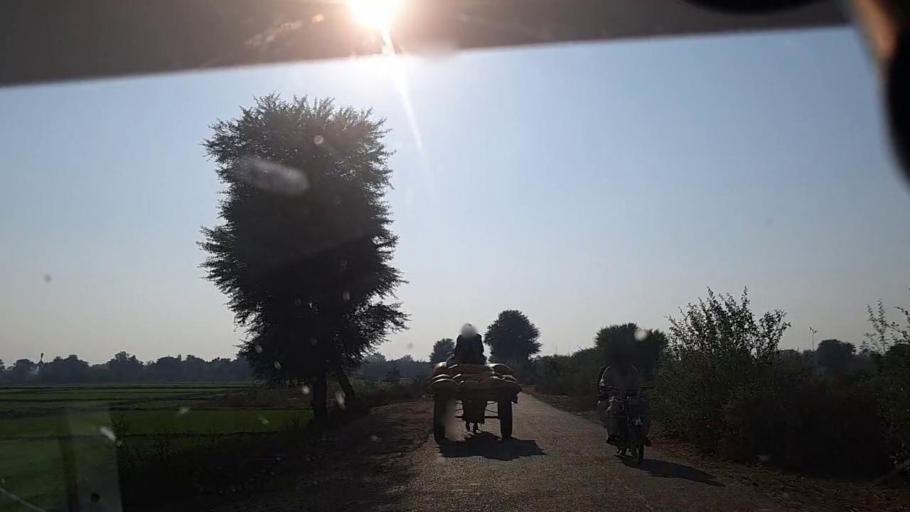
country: PK
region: Sindh
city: Sobhadero
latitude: 27.2404
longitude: 68.2839
